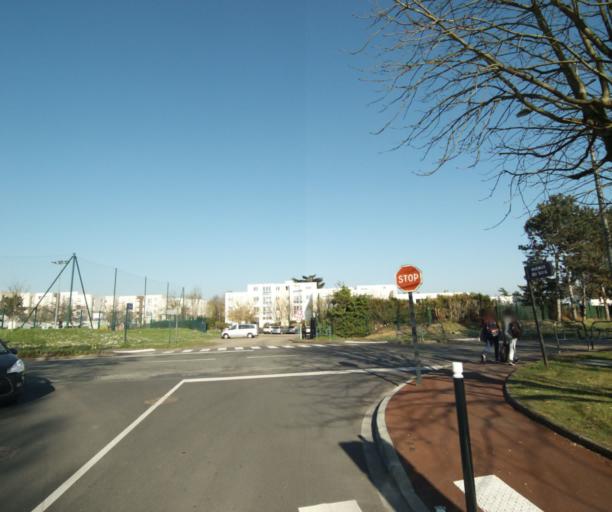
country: FR
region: Ile-de-France
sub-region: Departement du Val-d'Oise
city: Cergy
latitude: 49.0289
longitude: 2.0844
